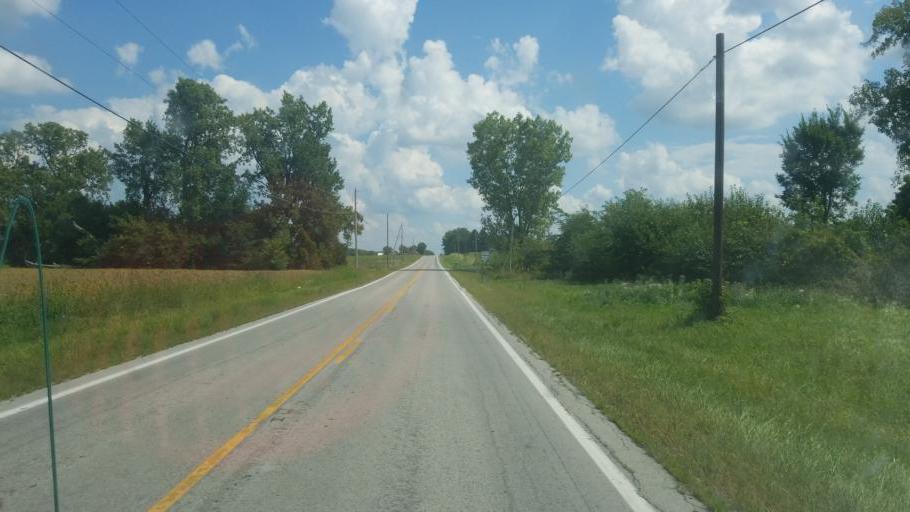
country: US
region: Ohio
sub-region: Hancock County
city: Arlington
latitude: 40.8922
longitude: -83.7261
